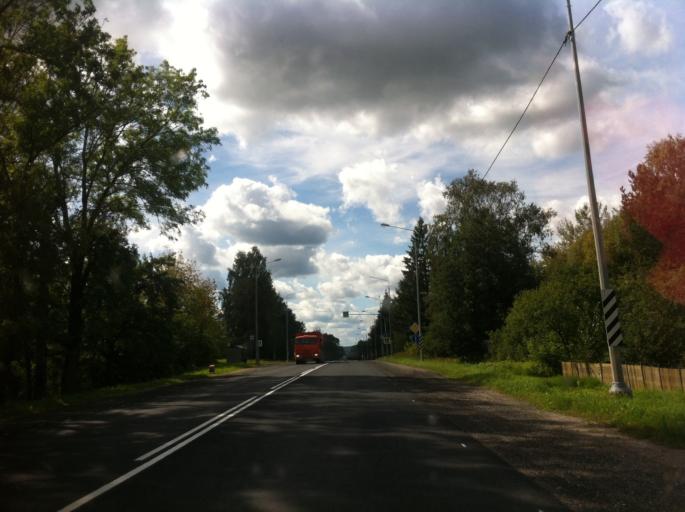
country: RU
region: Pskov
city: Izborsk
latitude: 57.7184
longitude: 27.9258
